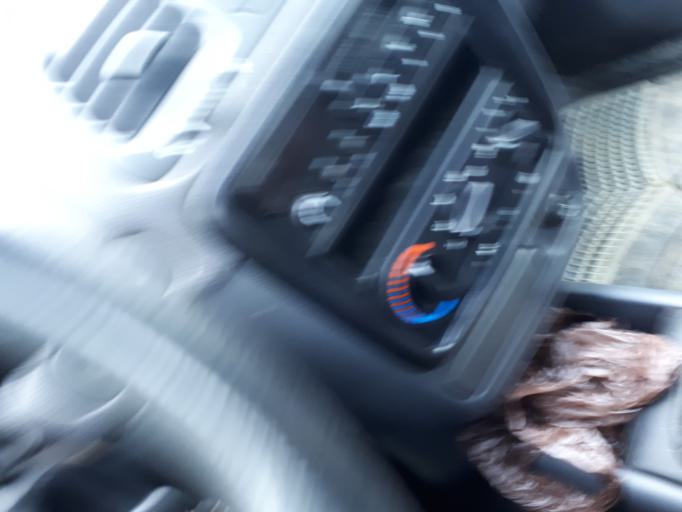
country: DZ
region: Tipaza
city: Douera
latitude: 36.7183
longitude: 2.9125
